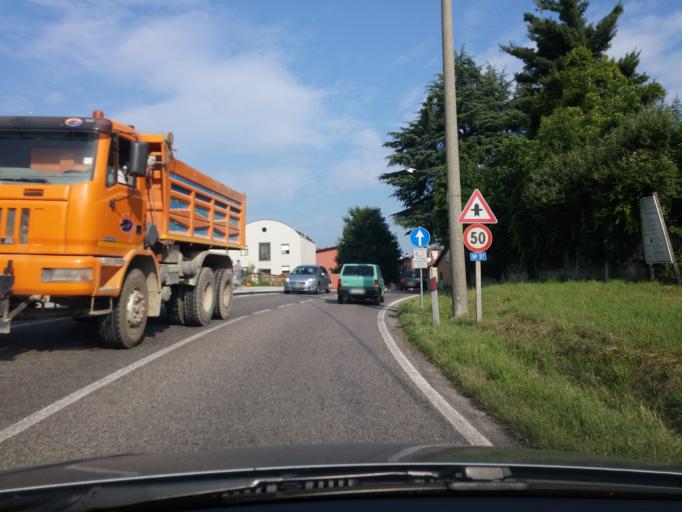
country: IT
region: Lombardy
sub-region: Provincia di Como
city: Cassina Rizzardi
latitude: 45.7502
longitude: 9.0337
